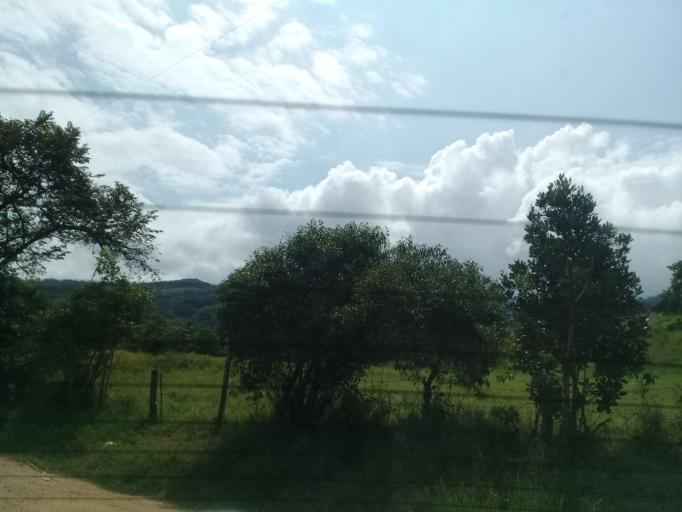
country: CO
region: Cundinamarca
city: Guaduas
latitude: 5.0248
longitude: -74.6090
